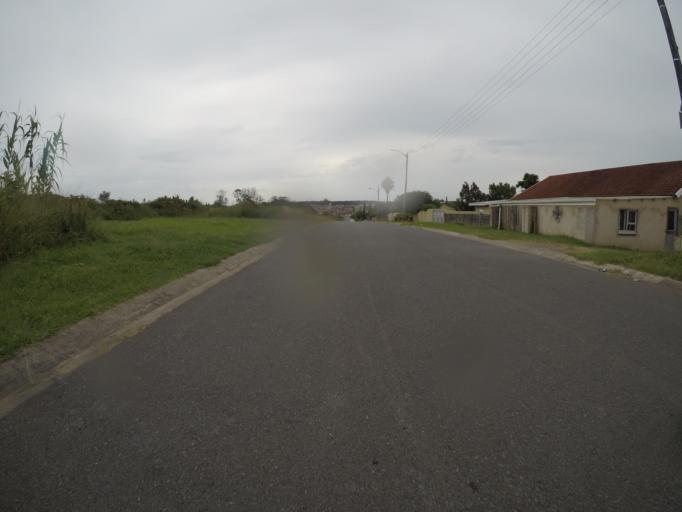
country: ZA
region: Eastern Cape
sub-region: Buffalo City Metropolitan Municipality
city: East London
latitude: -32.9993
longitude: 27.8501
